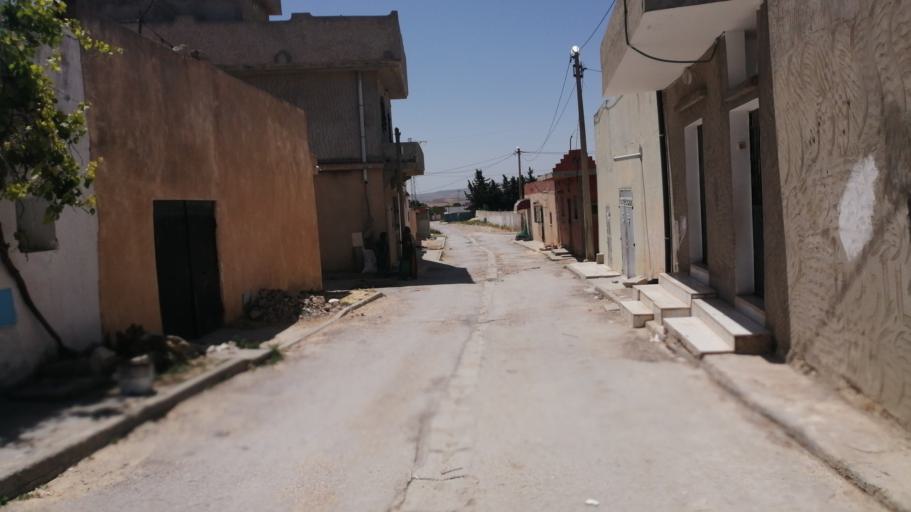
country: TN
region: Silyanah
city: Maktar
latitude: 35.8497
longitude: 9.2041
